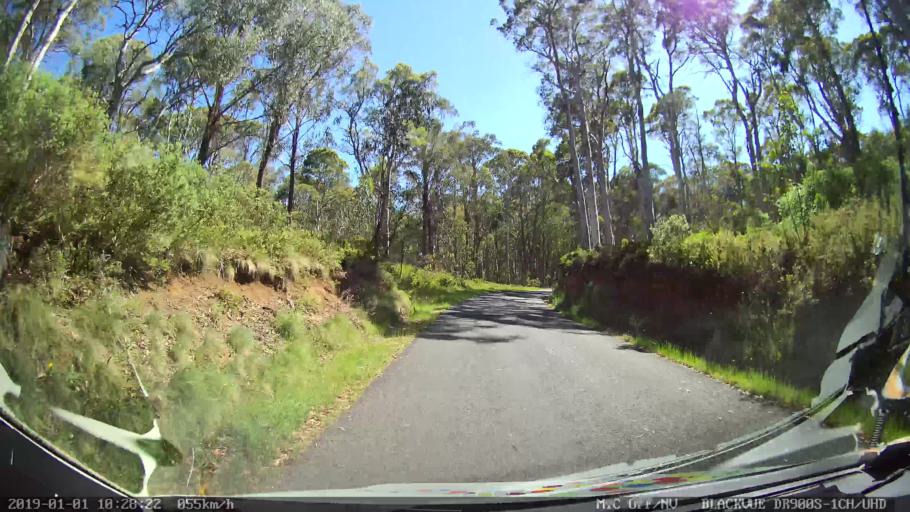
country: AU
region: New South Wales
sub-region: Snowy River
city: Jindabyne
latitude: -36.0607
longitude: 148.2400
